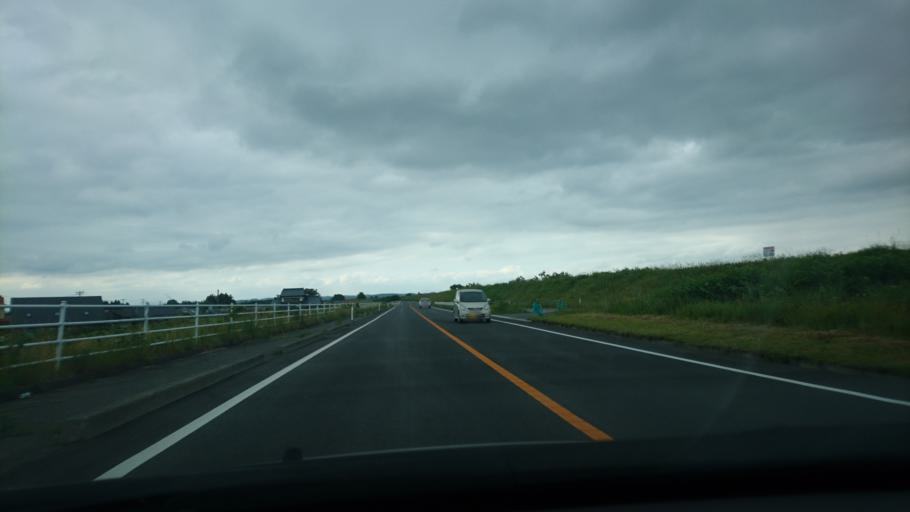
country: JP
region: Iwate
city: Ichinoseki
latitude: 38.7358
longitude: 141.1517
